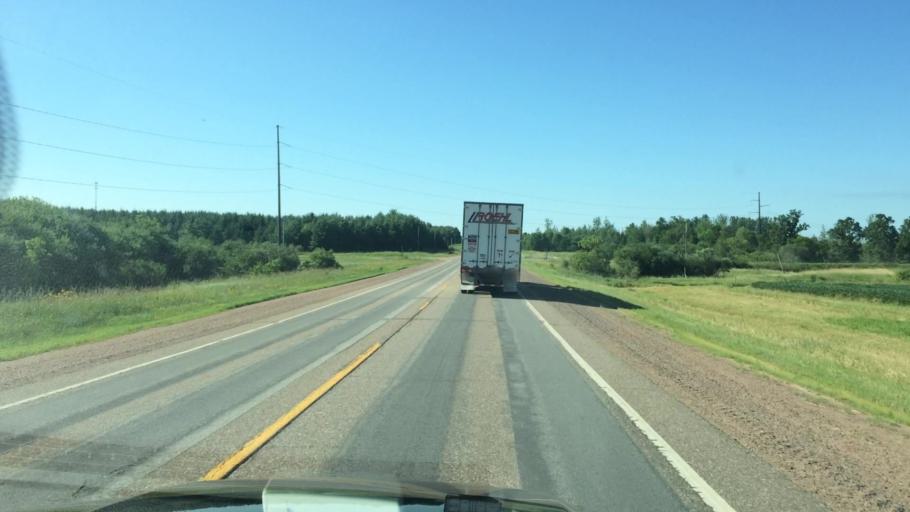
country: US
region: Wisconsin
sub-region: Marathon County
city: Athens
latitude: 44.9327
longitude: -90.0790
